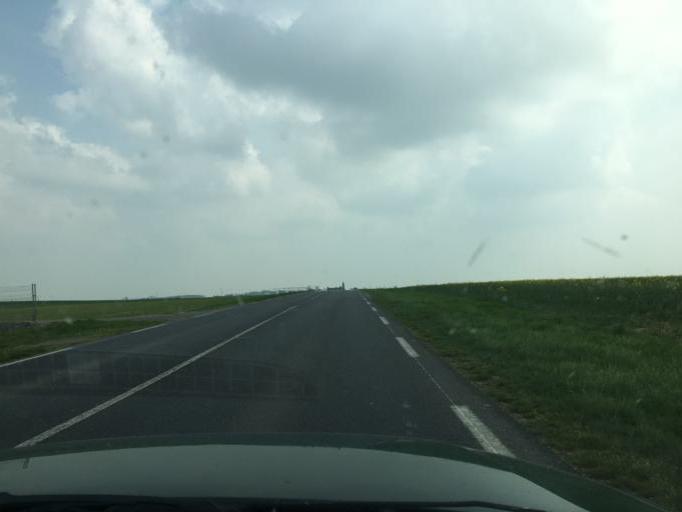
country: FR
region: Centre
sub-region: Departement du Loir-et-Cher
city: Ouzouer-le-Marche
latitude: 47.9073
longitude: 1.4951
